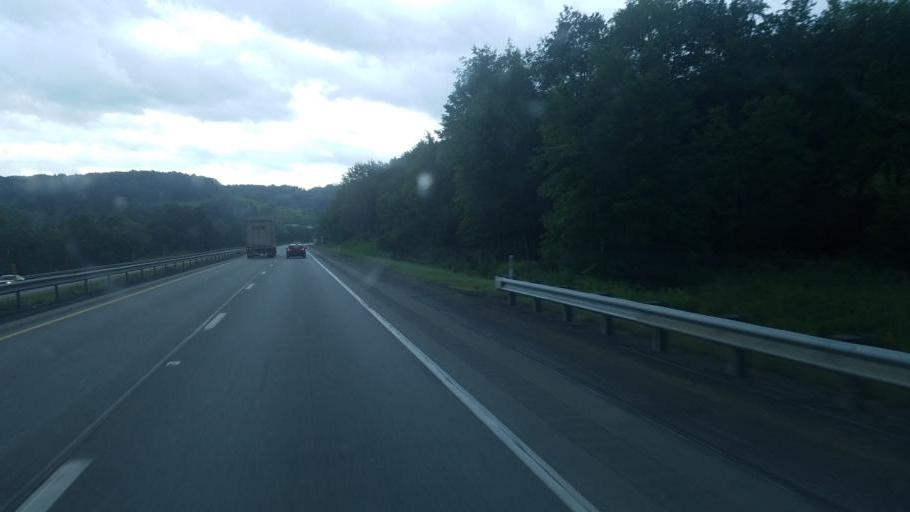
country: US
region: Pennsylvania
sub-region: Butler County
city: Zelienople
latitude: 40.8540
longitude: -80.1058
